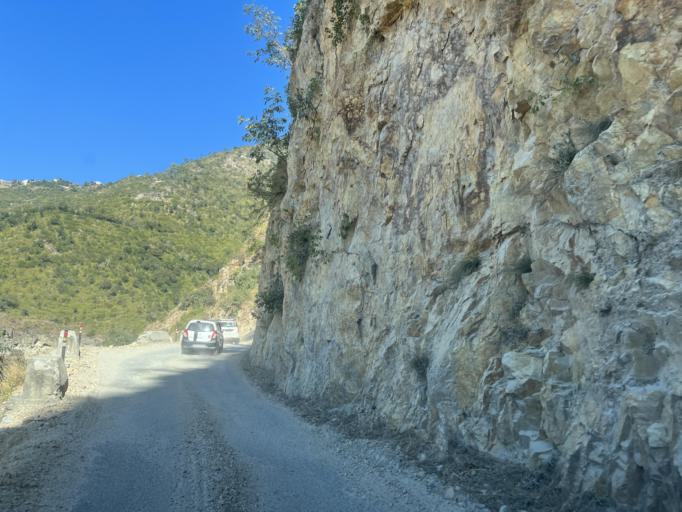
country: IN
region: Uttarakhand
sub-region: Naini Tal
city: Naini Tal
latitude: 29.5081
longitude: 79.4536
